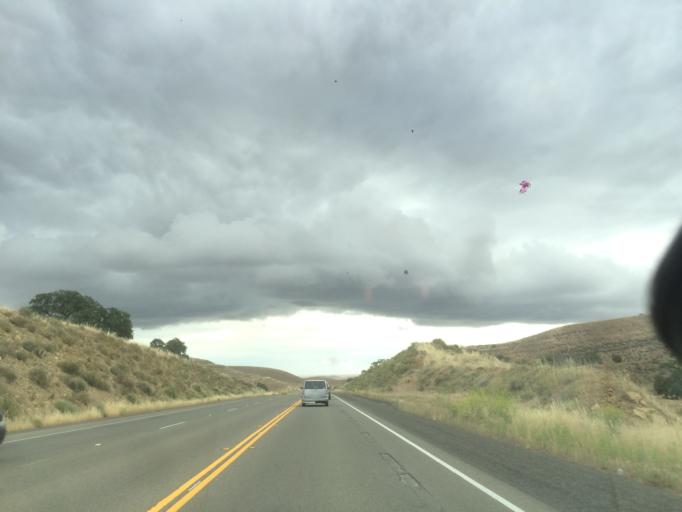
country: US
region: California
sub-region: Kings County
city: Avenal
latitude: 35.7730
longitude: -120.1623
